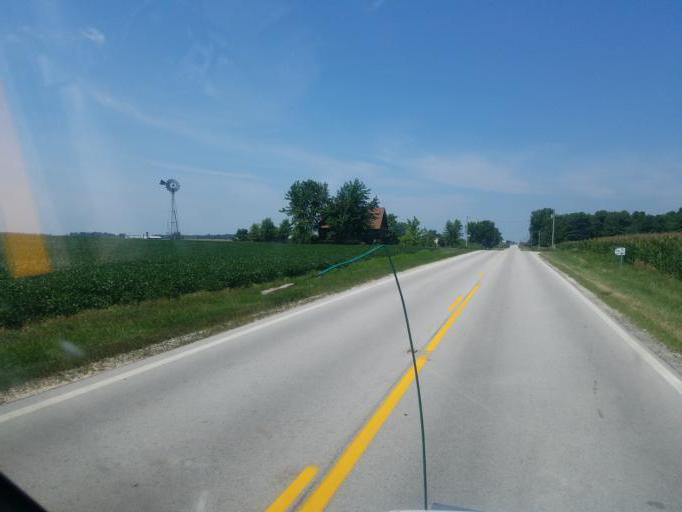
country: US
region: Ohio
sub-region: Auglaize County
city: New Bremen
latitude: 40.4267
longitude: -84.4337
